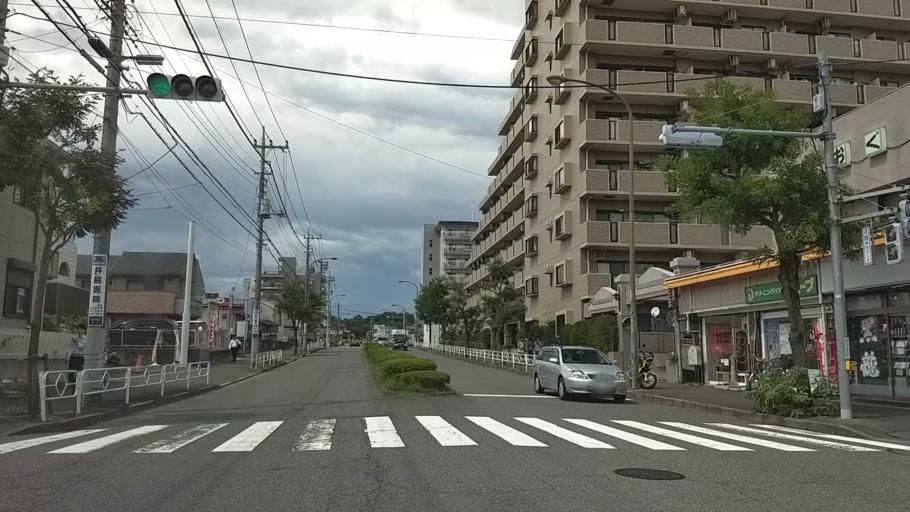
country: JP
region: Tokyo
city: Hachioji
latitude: 35.6418
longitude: 139.3075
